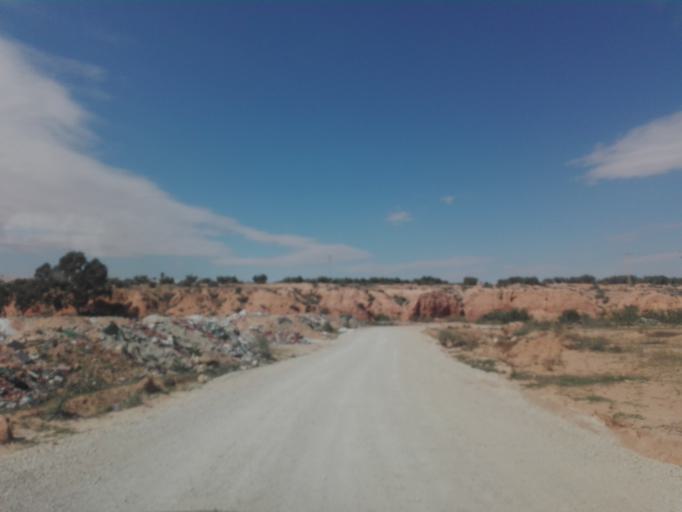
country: TN
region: Safaqis
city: Sfax
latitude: 34.6861
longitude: 10.5608
